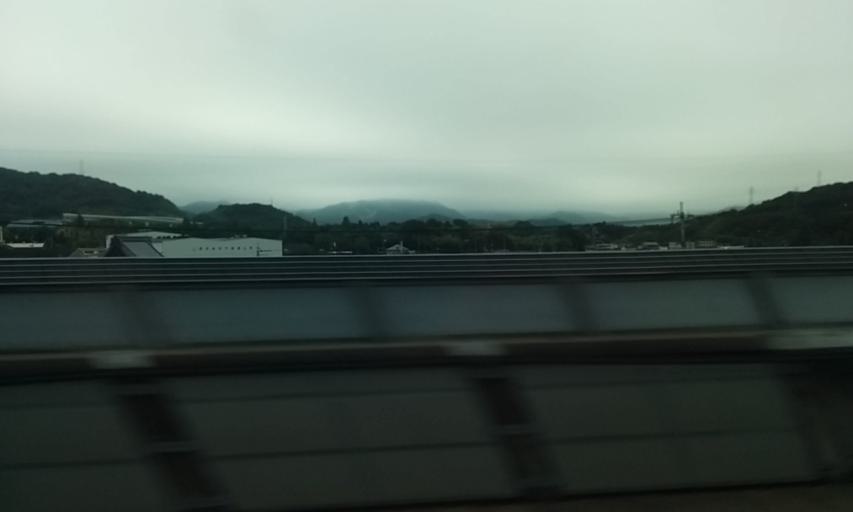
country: JP
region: Hyogo
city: Aioi
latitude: 34.8179
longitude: 134.4949
